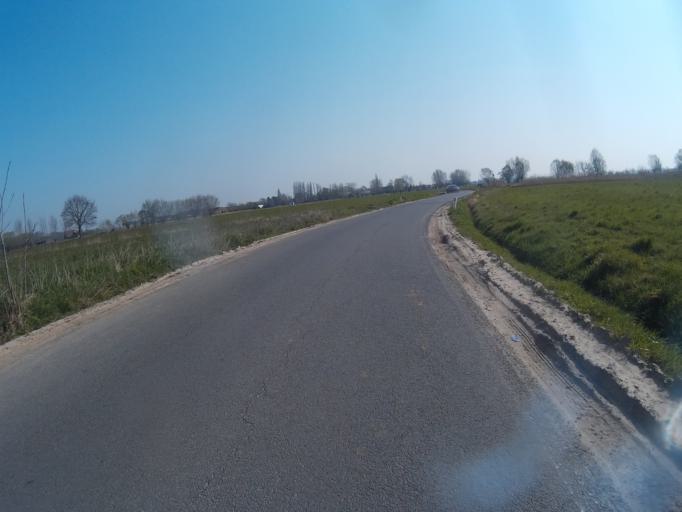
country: BE
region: Flanders
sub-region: Provincie Oost-Vlaanderen
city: Zomergem
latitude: 51.1100
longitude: 3.5163
